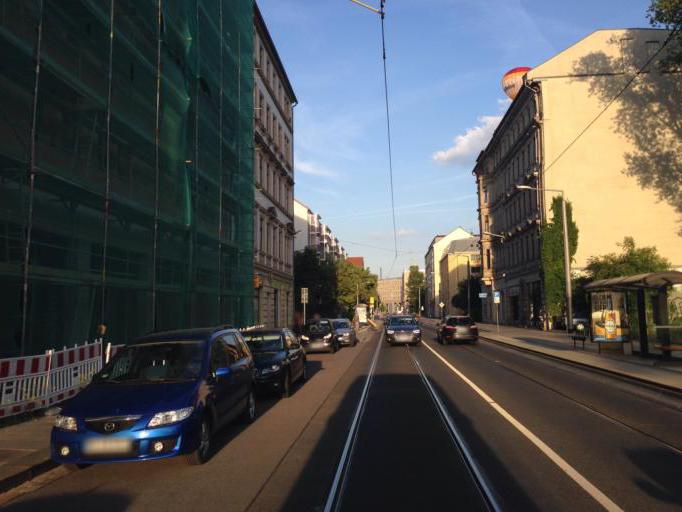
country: DE
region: Saxony
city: Dresden
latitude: 51.0530
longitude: 13.7261
